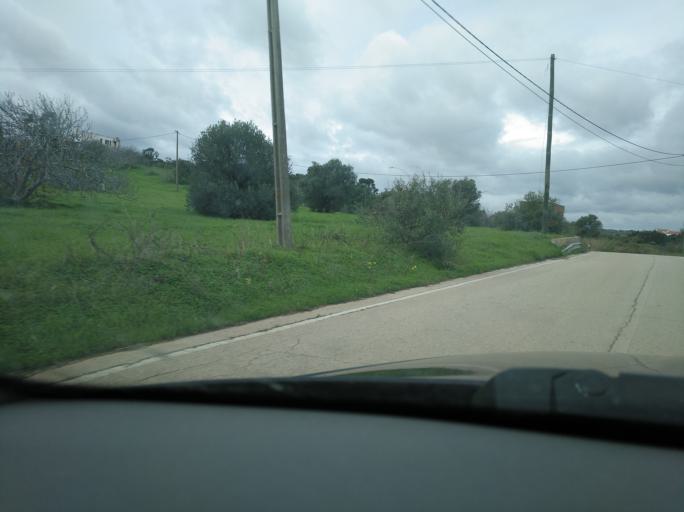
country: PT
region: Faro
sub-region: Castro Marim
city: Castro Marim
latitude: 37.2156
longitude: -7.4869
